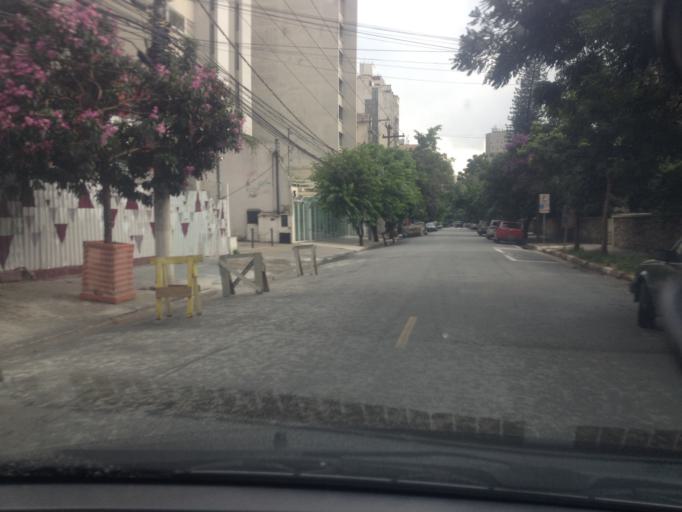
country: BR
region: Sao Paulo
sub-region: Sao Paulo
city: Sao Paulo
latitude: -23.5628
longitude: -46.6980
